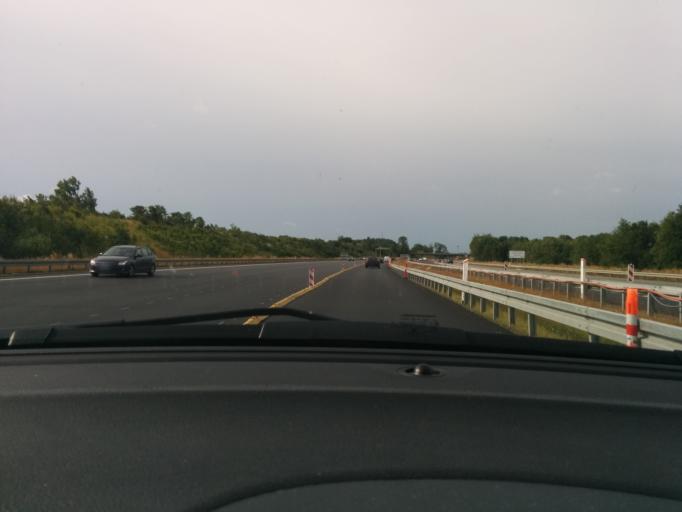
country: DK
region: Zealand
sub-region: Solrod Kommune
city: Solrod
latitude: 55.5262
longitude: 12.1959
